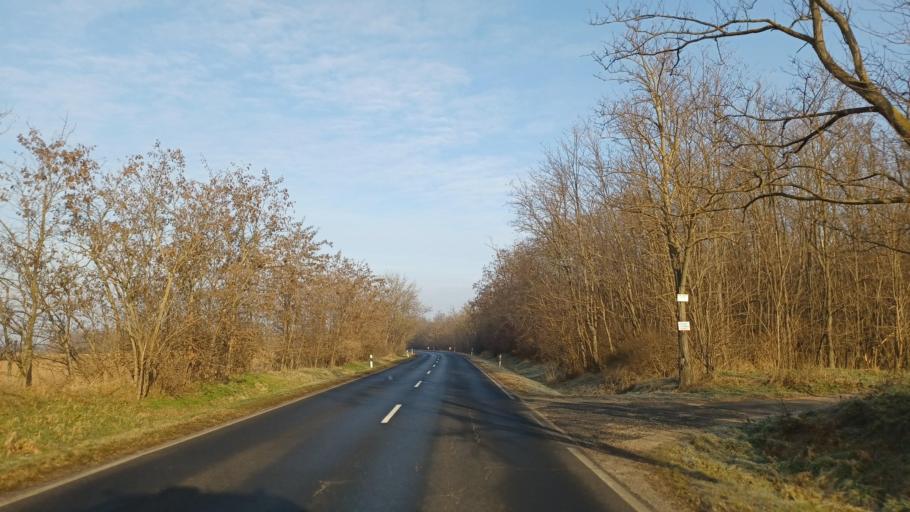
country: HU
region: Fejer
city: Cece
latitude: 46.7357
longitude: 18.6573
